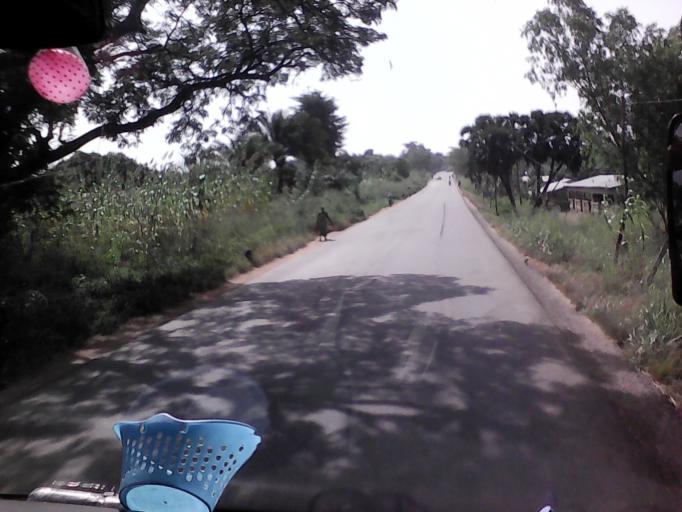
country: TG
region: Centrale
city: Sokode
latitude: 8.8370
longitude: 1.0762
